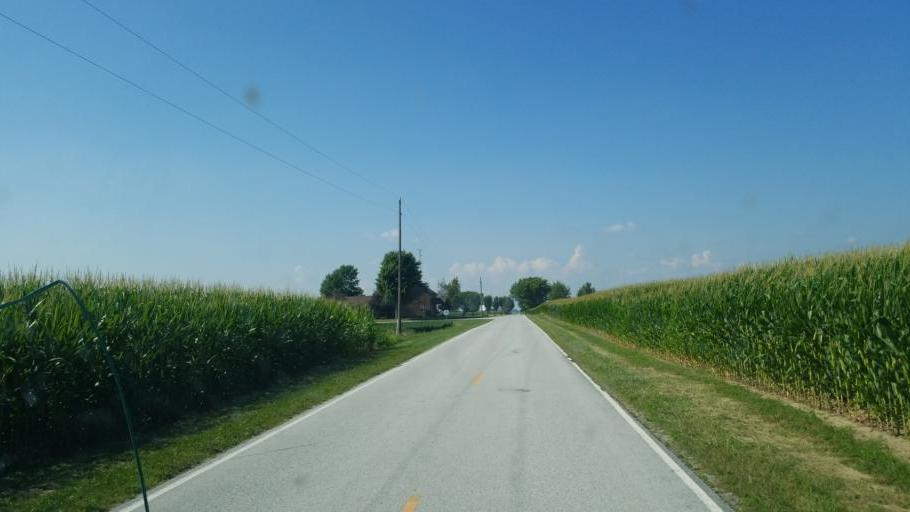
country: US
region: Ohio
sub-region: Hardin County
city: Forest
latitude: 40.7111
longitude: -83.4958
